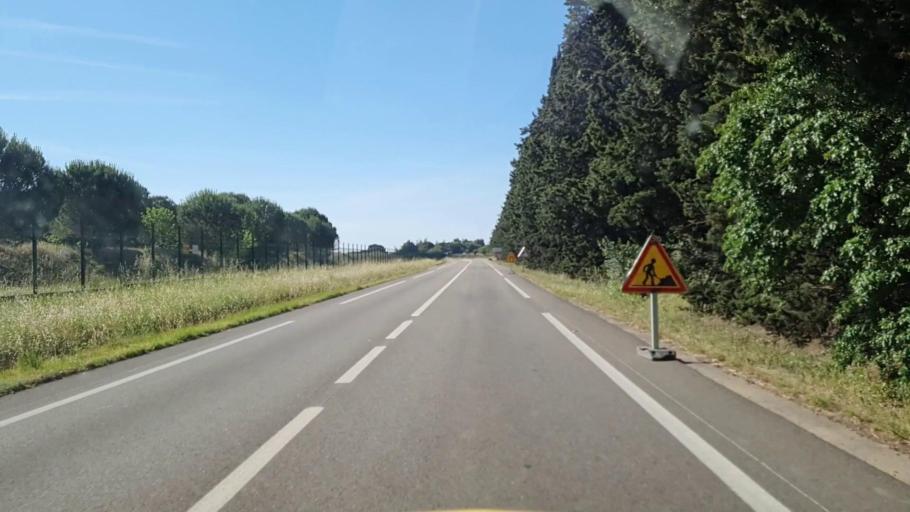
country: FR
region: Languedoc-Roussillon
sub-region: Departement du Gard
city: Garons
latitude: 43.7502
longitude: 4.4077
